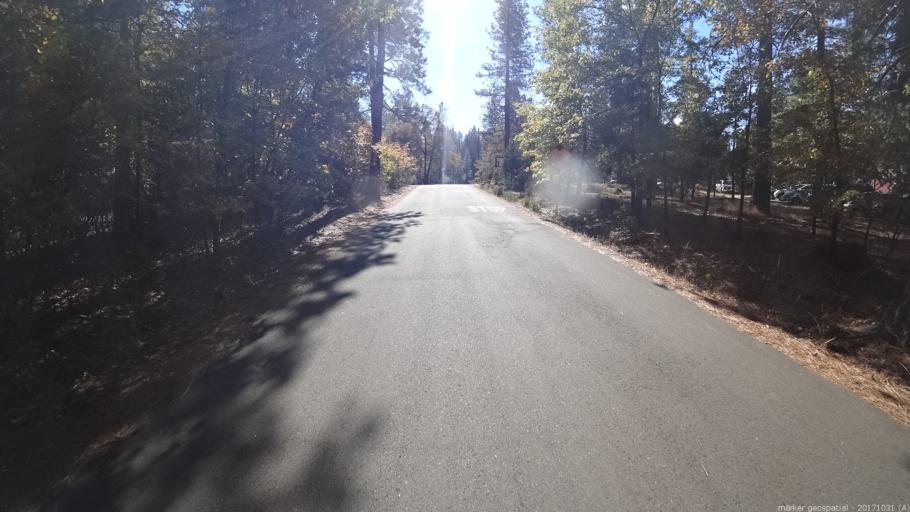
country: US
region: California
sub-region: Shasta County
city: Shingletown
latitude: 40.5134
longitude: -121.9361
